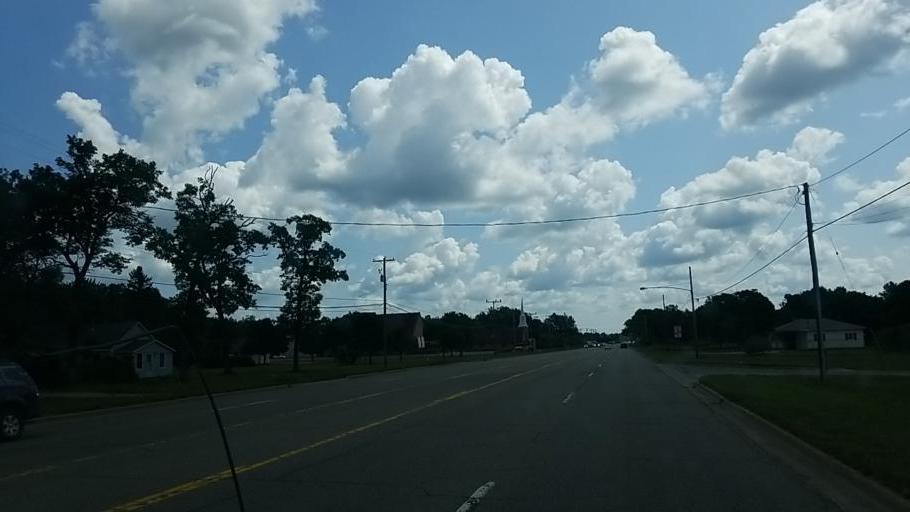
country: US
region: Michigan
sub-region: Muskegon County
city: Wolf Lake
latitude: 43.2344
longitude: -86.1426
